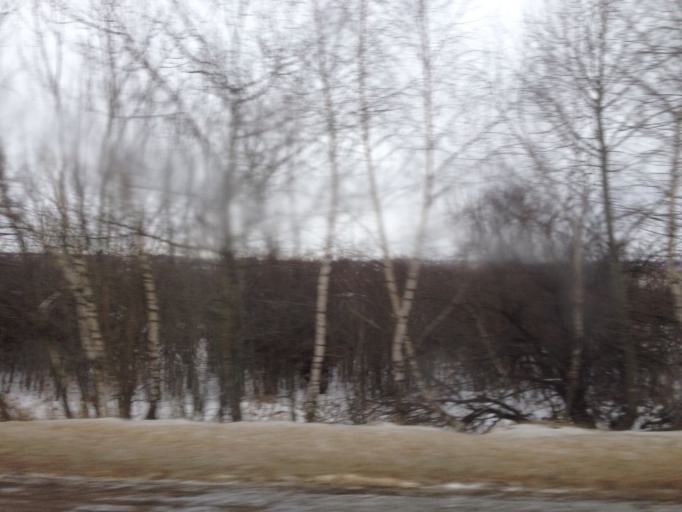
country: RU
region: Tula
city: Kamenetskiy
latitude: 53.9935
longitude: 38.2113
